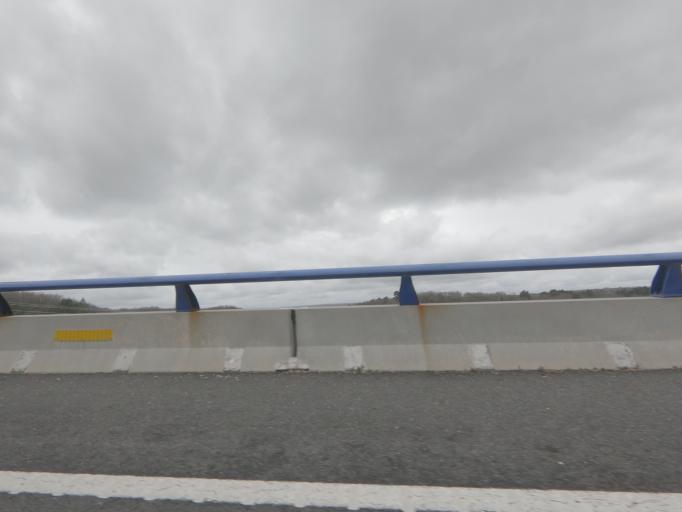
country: ES
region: Castille and Leon
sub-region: Provincia de Salamanca
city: Puerto de Bejar
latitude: 40.3558
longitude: -5.8410
